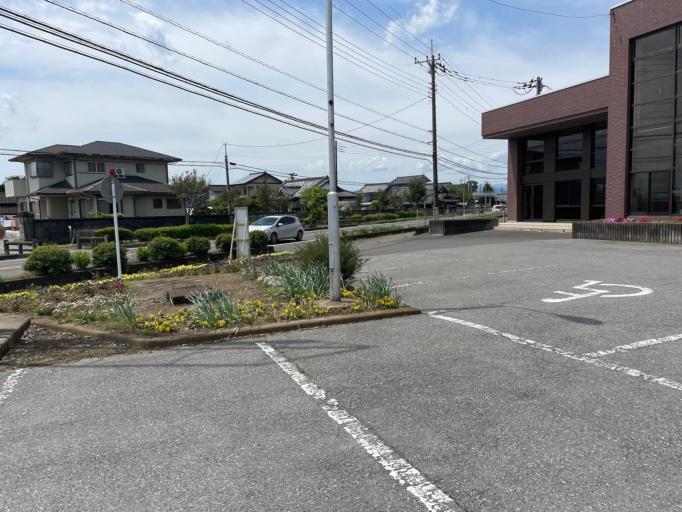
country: JP
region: Tochigi
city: Mibu
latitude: 36.4483
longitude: 139.7796
